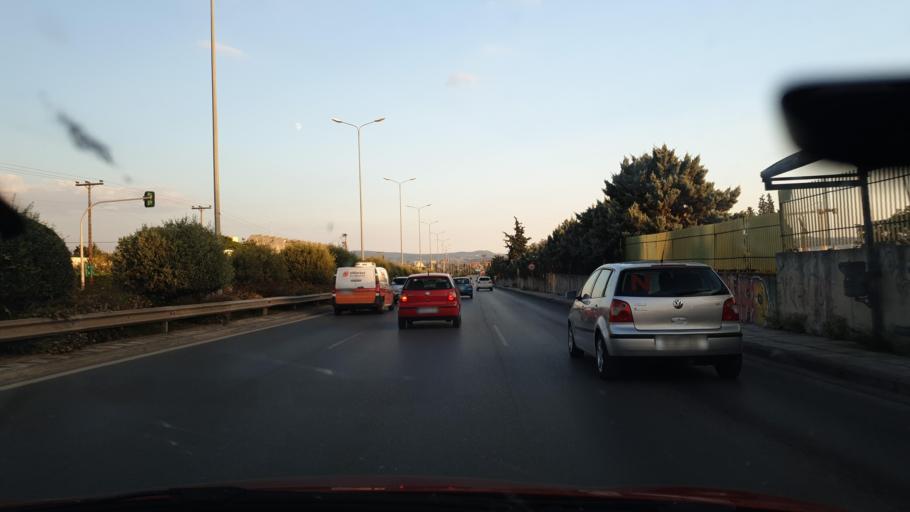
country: GR
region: Central Macedonia
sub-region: Nomos Thessalonikis
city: Kalamaria
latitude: 40.5583
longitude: 22.9776
